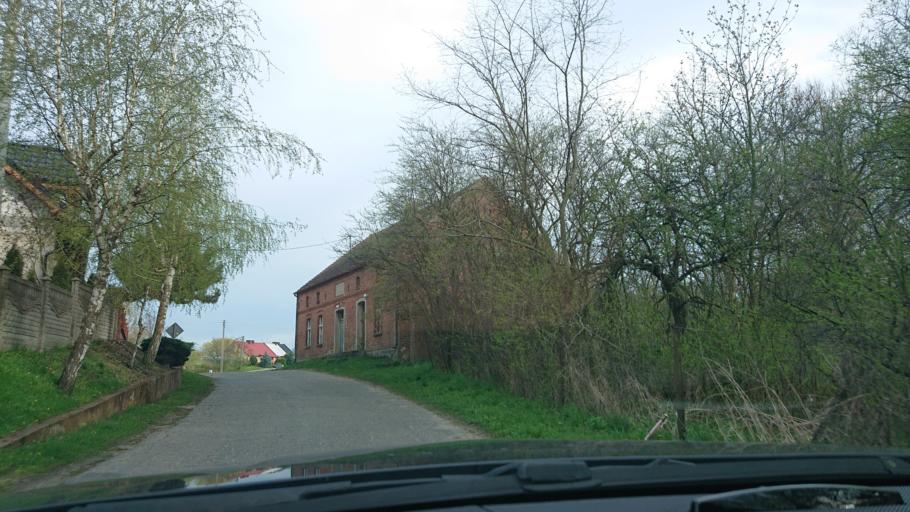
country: PL
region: Greater Poland Voivodeship
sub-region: Powiat gnieznienski
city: Lubowo
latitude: 52.5747
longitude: 17.4714
